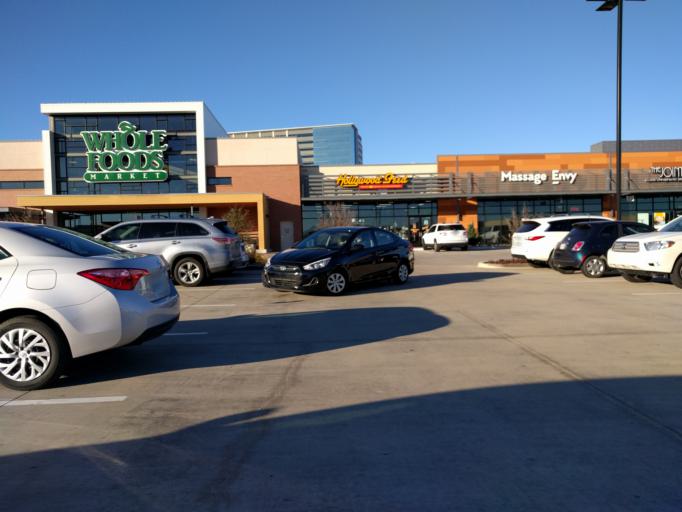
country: US
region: Texas
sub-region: Collin County
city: Plano
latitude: 32.9982
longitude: -96.6983
